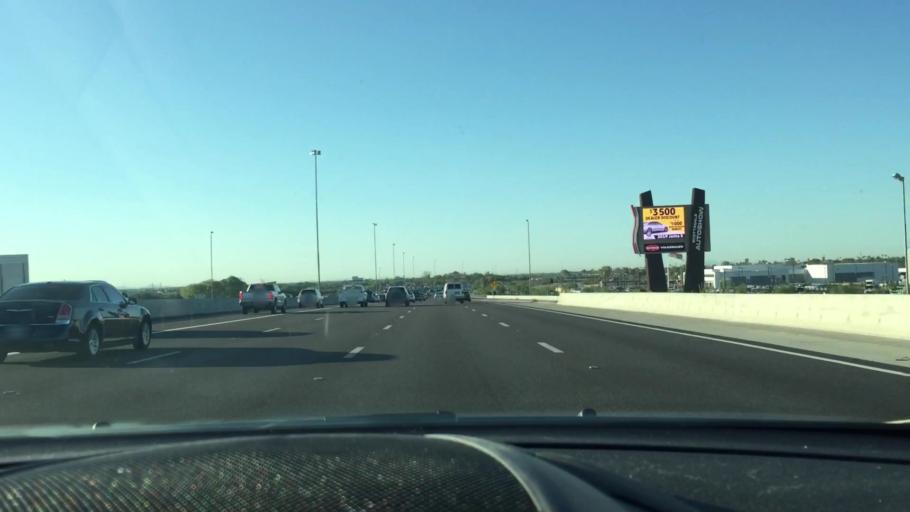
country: US
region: Arizona
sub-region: Maricopa County
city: Scottsdale
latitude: 33.4932
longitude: -111.8885
